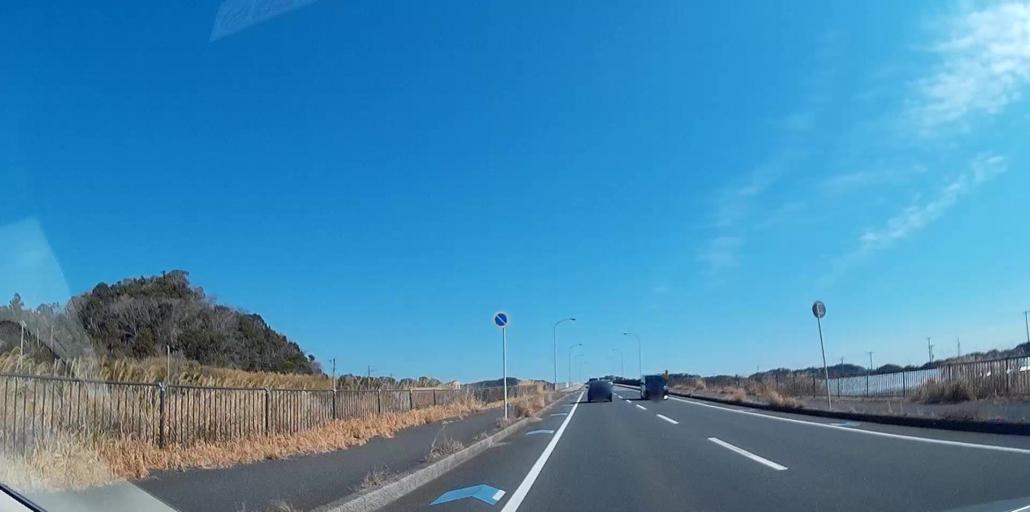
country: JP
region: Chiba
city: Tateyama
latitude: 35.0383
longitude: 139.8394
